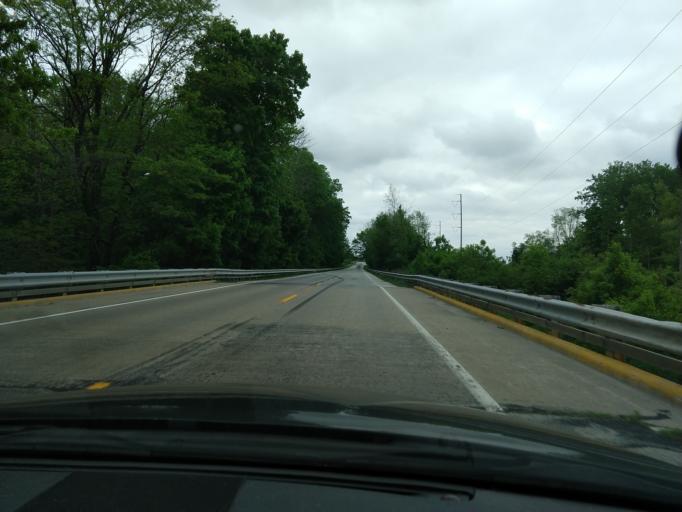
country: US
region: Indiana
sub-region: Hamilton County
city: Noblesville
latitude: 40.0506
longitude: -85.9370
